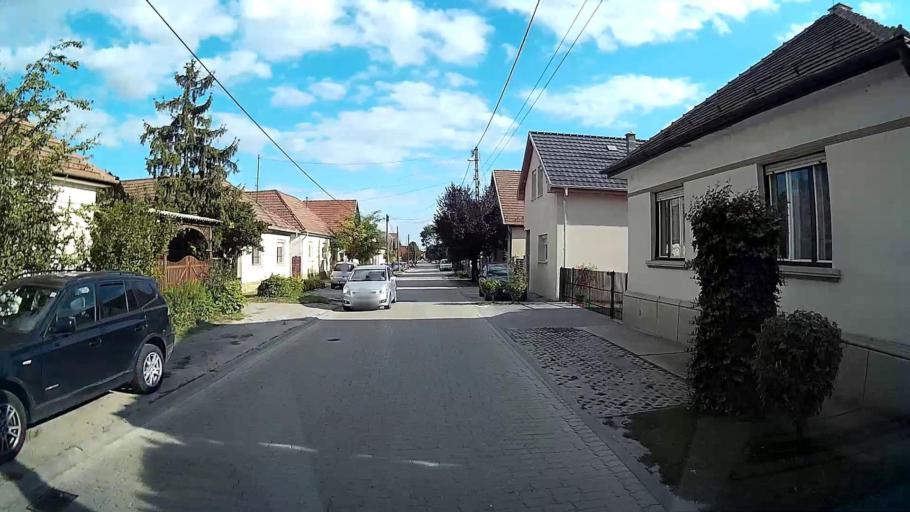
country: HU
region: Pest
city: Pilisvorosvar
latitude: 47.6244
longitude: 18.9024
